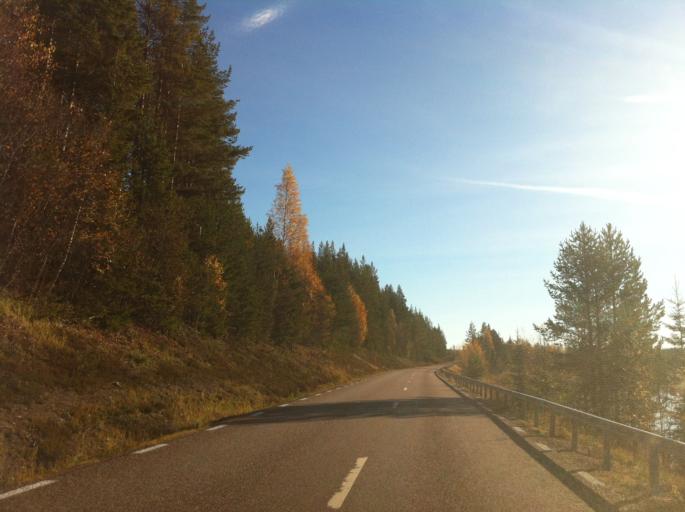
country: NO
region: Hedmark
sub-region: Trysil
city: Innbygda
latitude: 61.8242
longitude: 12.8837
